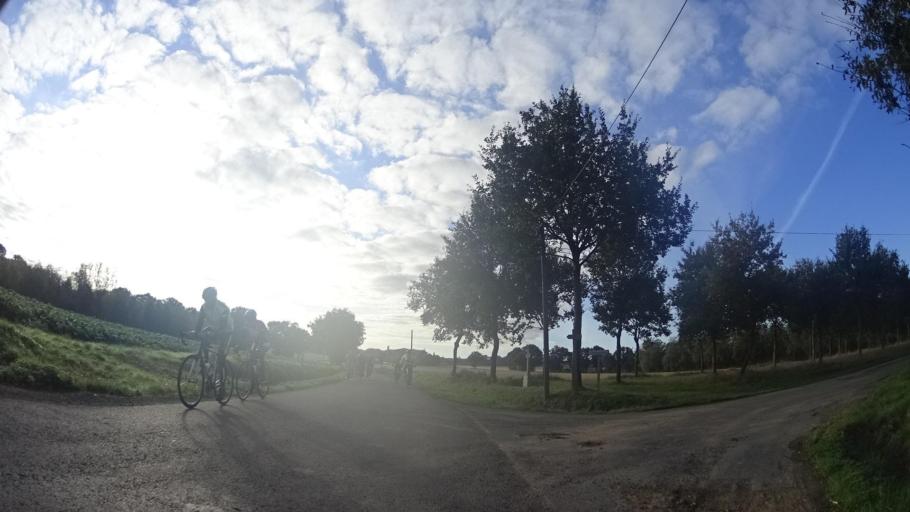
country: FR
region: Brittany
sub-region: Departement des Cotes-d'Armor
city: Evran
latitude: 48.3544
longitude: -1.9429
